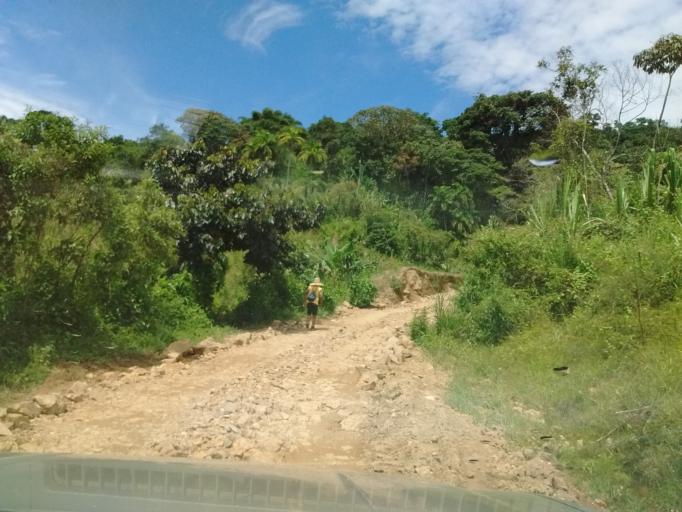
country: CO
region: Cauca
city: Morales
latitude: 2.6733
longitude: -76.7640
